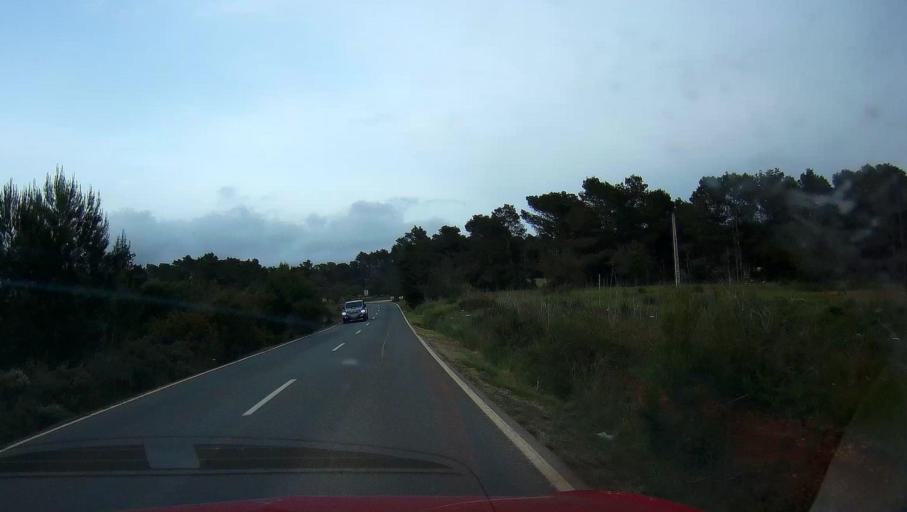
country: ES
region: Balearic Islands
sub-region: Illes Balears
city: Sant Joan de Labritja
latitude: 39.0581
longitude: 1.4625
